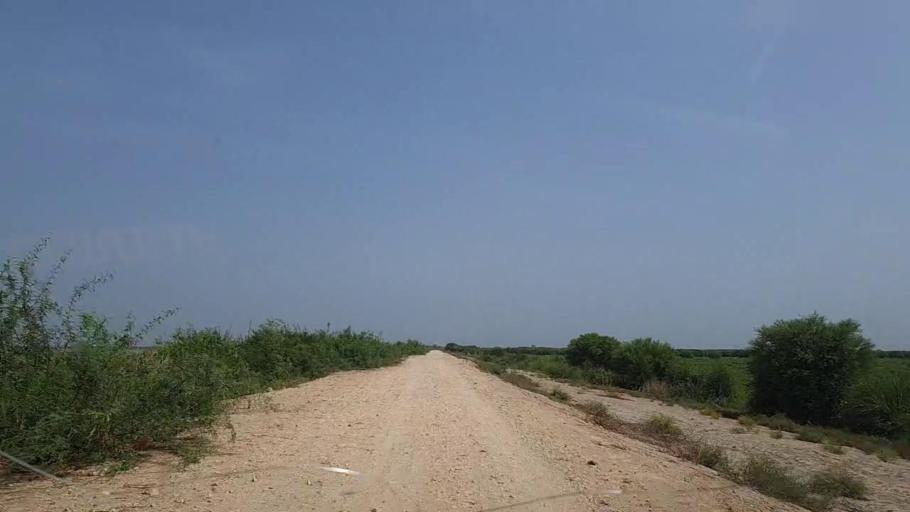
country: PK
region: Sindh
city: Ghotki
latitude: 28.1042
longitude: 69.3980
